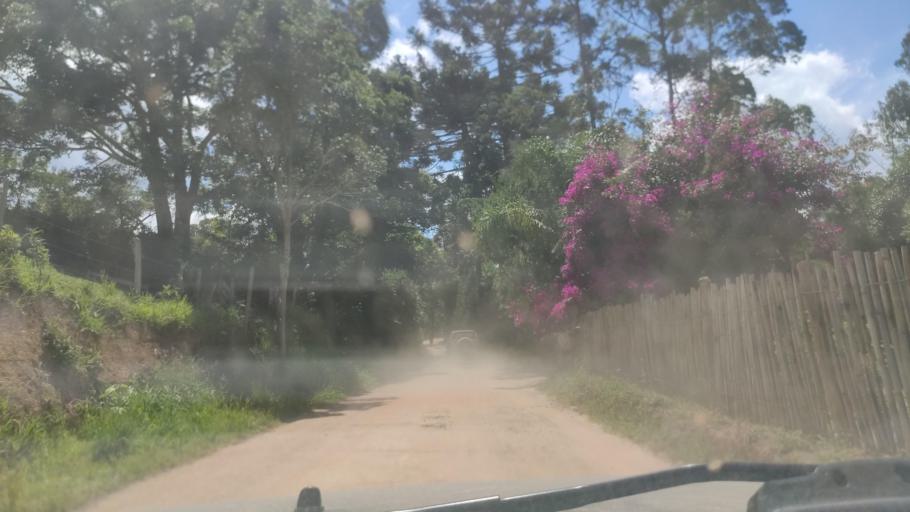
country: BR
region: Minas Gerais
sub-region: Cambui
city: Cambui
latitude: -22.7001
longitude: -46.0068
